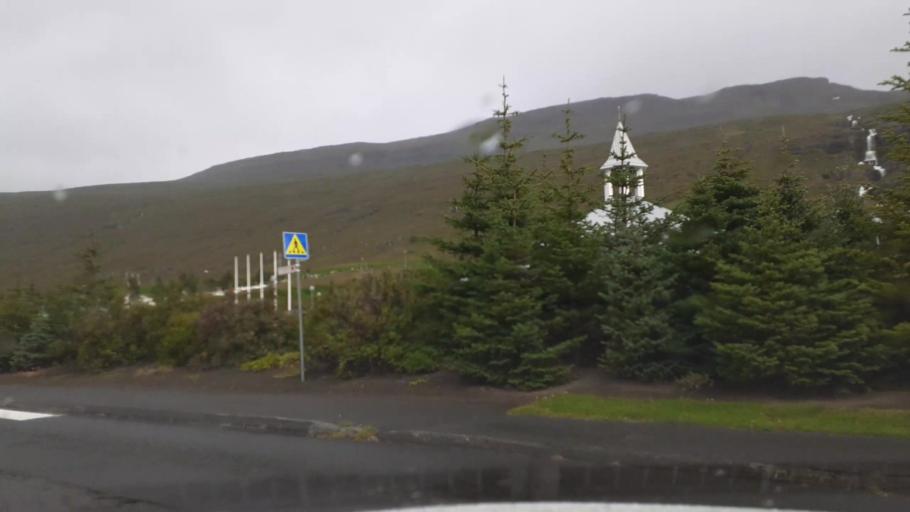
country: IS
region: East
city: Eskifjoerdur
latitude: 65.0781
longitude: -14.0336
